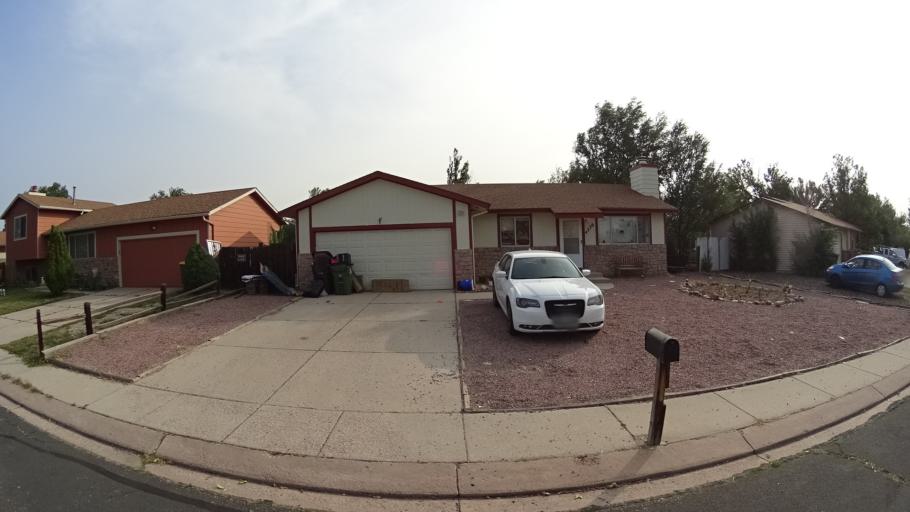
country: US
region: Colorado
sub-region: El Paso County
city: Stratmoor
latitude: 38.8007
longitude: -104.7488
